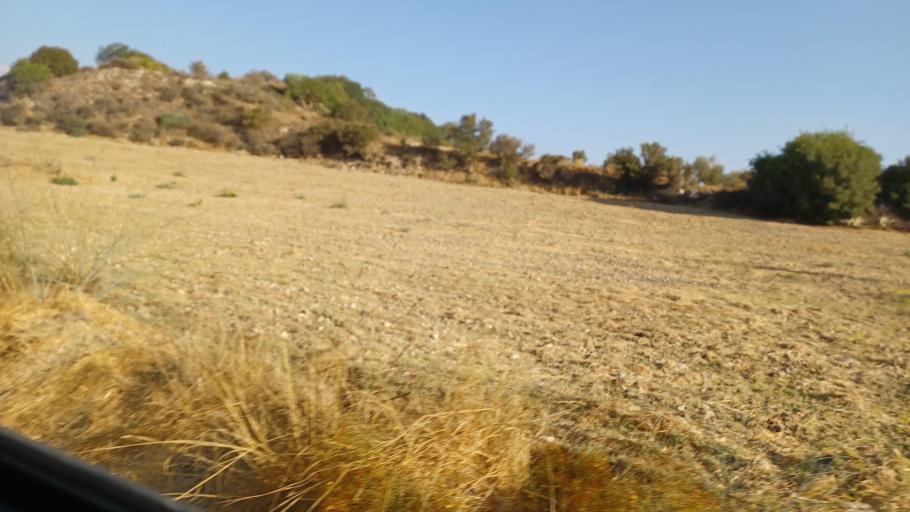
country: CY
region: Pafos
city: Tala
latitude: 34.9243
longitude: 32.4962
